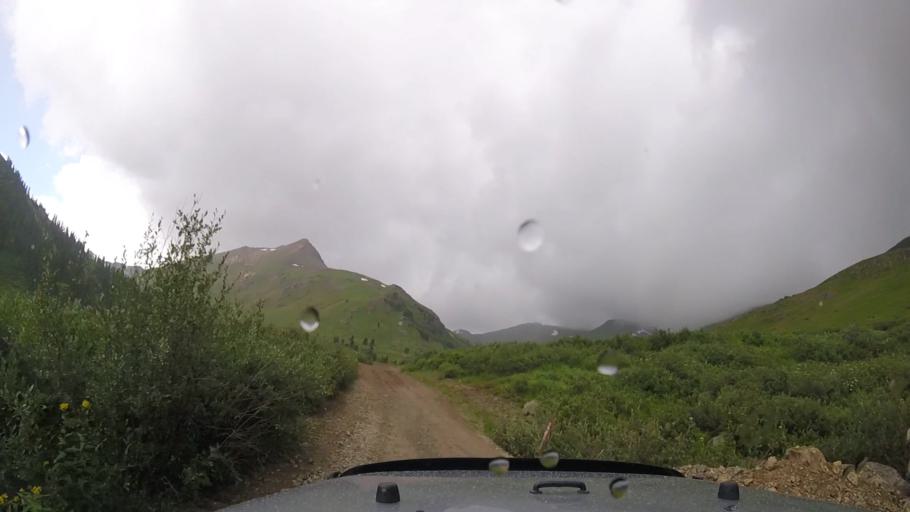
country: US
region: Colorado
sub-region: Ouray County
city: Ouray
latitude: 37.9321
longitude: -107.5842
